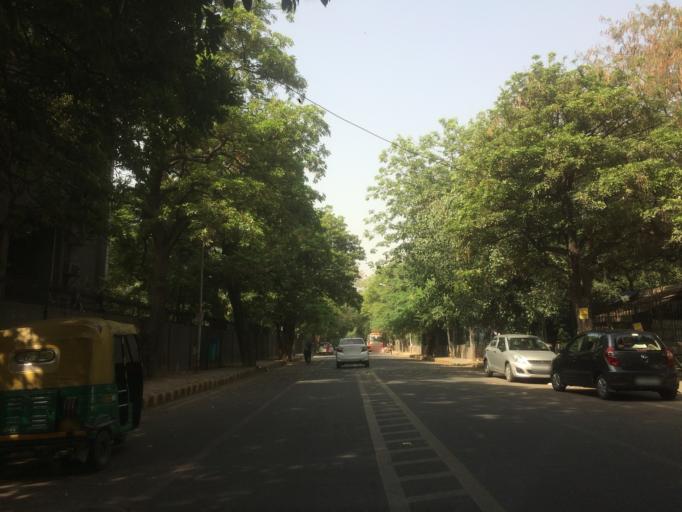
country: IN
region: NCT
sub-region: Central Delhi
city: Karol Bagh
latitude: 28.6325
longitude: 77.2015
